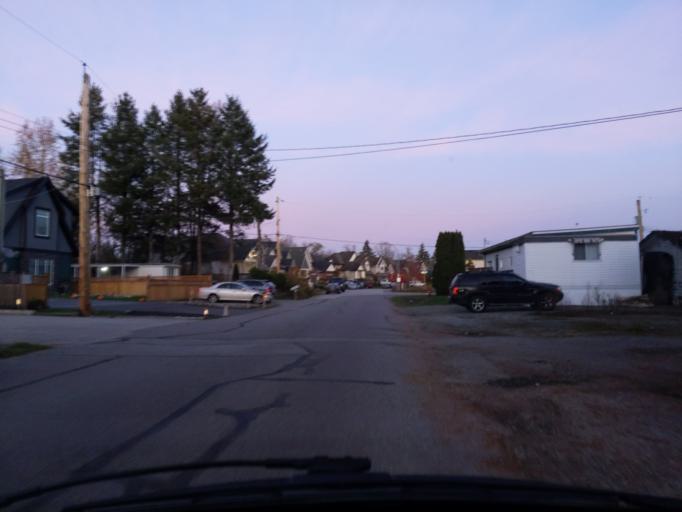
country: CA
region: British Columbia
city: Walnut Grove
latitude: 49.1826
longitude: -122.6610
